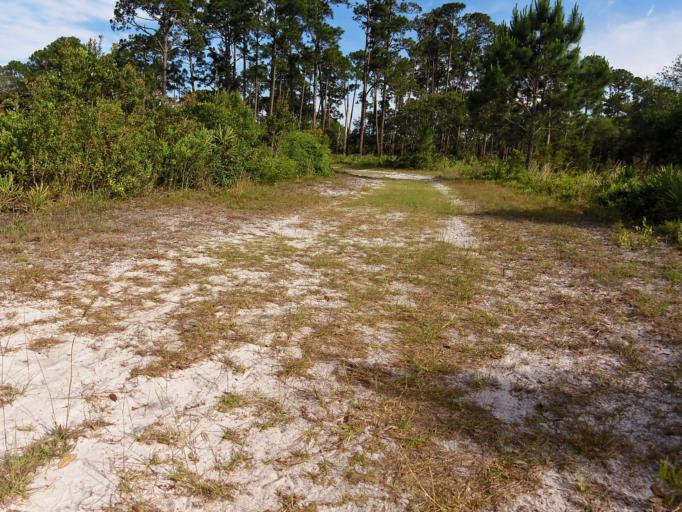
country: US
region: Florida
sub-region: Saint Johns County
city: Villano Beach
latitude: 30.0271
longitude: -81.3404
